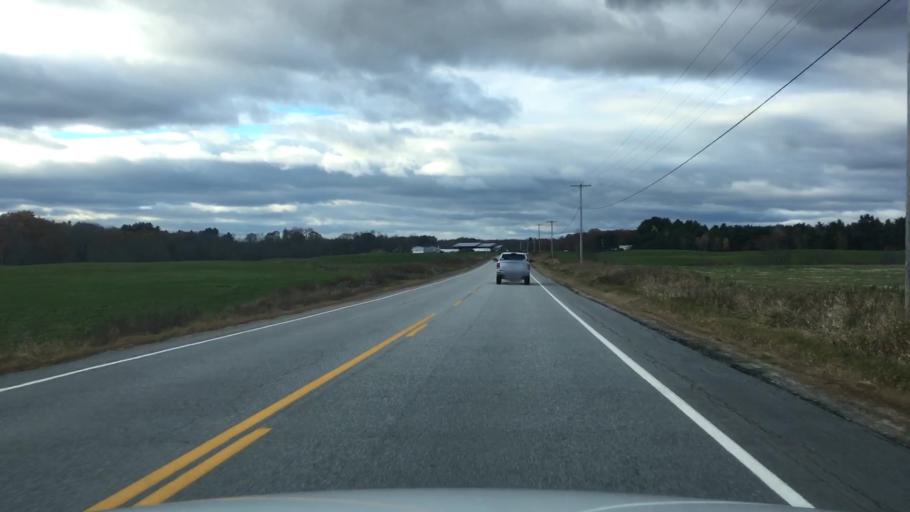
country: US
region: Maine
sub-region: Androscoggin County
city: Leeds
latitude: 44.3331
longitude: -70.1270
